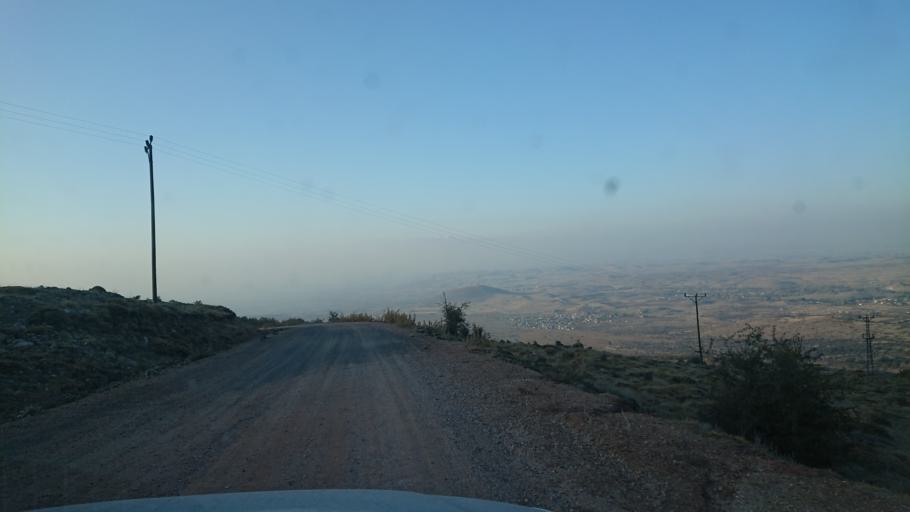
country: TR
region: Aksaray
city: Taspinar
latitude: 38.1670
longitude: 34.1808
